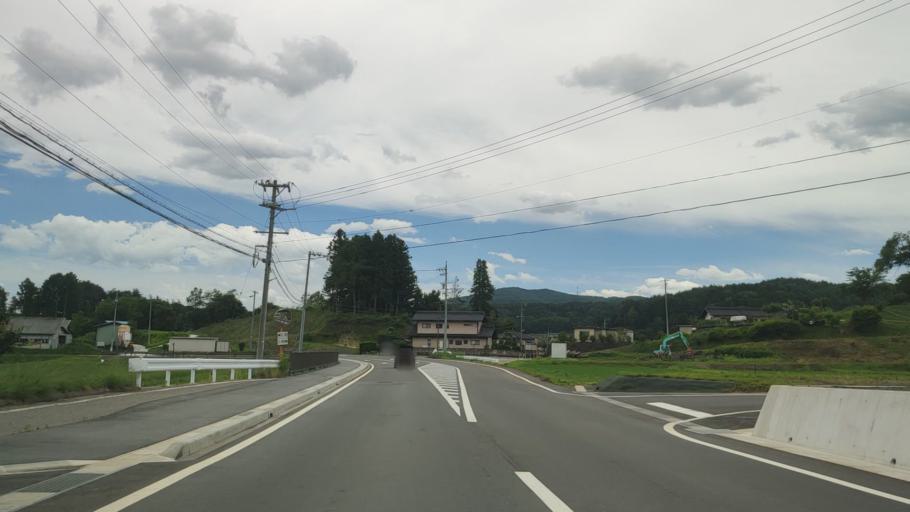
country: JP
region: Nagano
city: Kamimaruko
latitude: 36.2781
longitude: 138.2925
